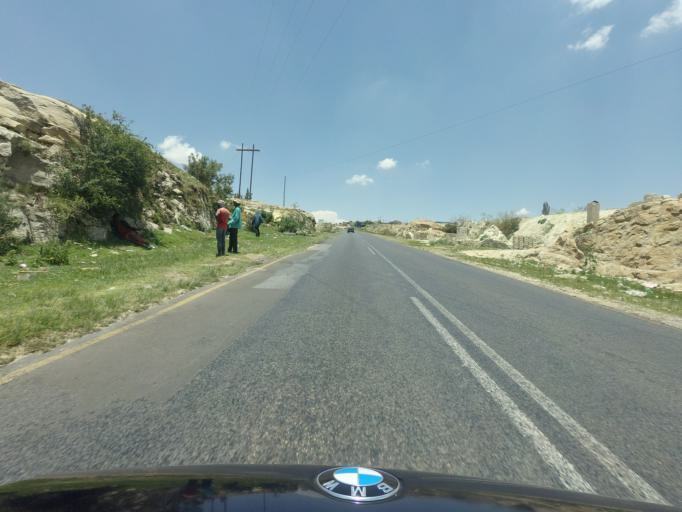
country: LS
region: Berea
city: Teyateyaneng
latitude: -29.1537
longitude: 27.6752
